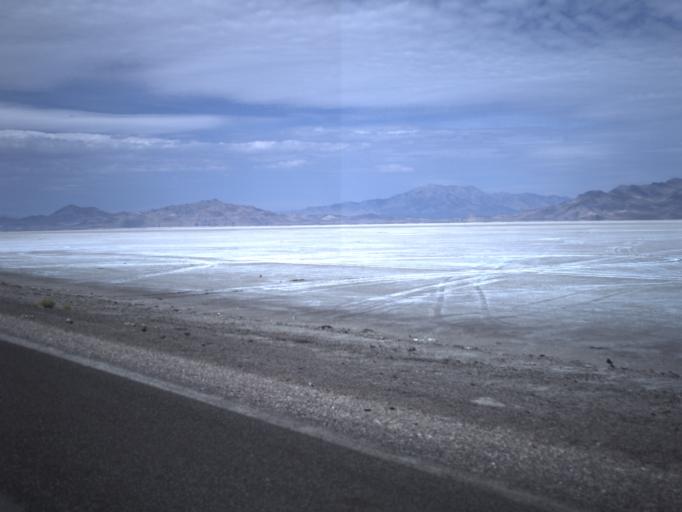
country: US
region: Utah
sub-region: Tooele County
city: Wendover
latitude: 40.7361
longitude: -113.6920
